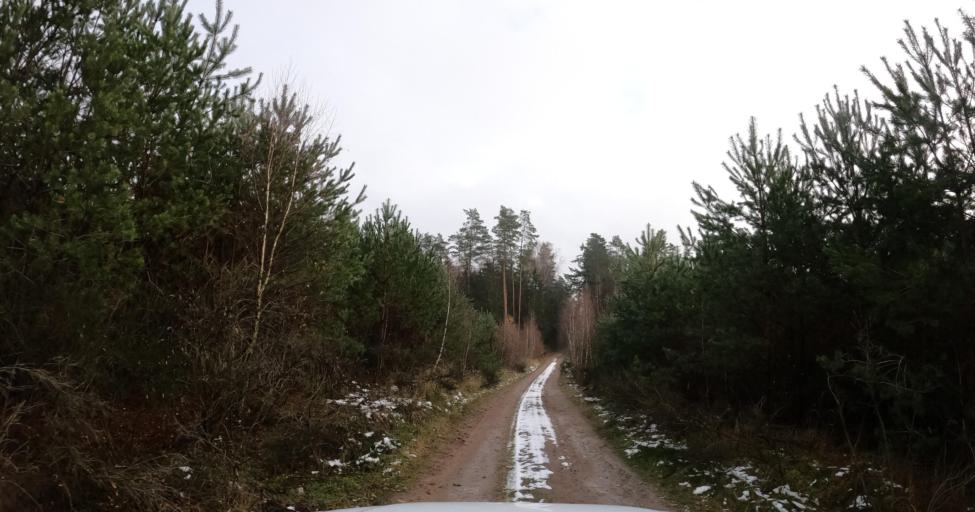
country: PL
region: West Pomeranian Voivodeship
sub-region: Powiat swidwinski
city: Rabino
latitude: 53.9080
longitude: 15.8840
